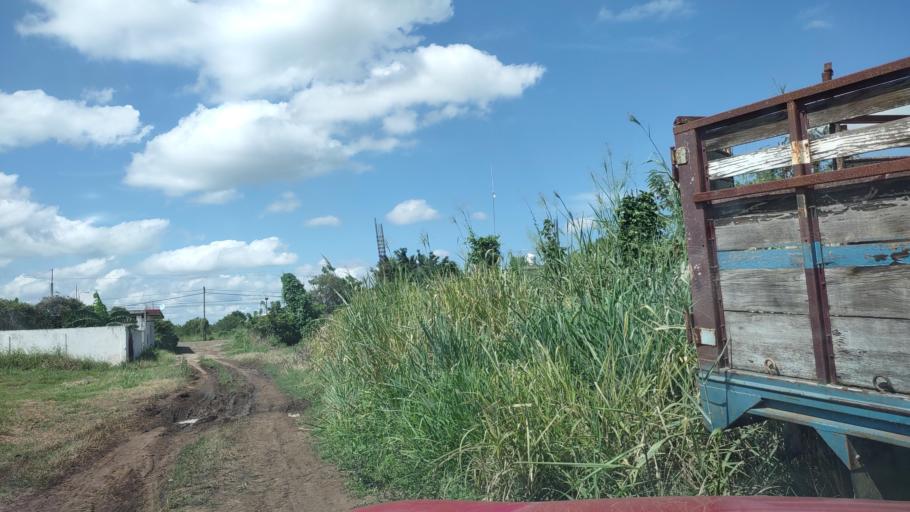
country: MX
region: Veracruz
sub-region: Martinez de la Torre
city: La Union Paso Largo
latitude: 20.1321
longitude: -96.9961
